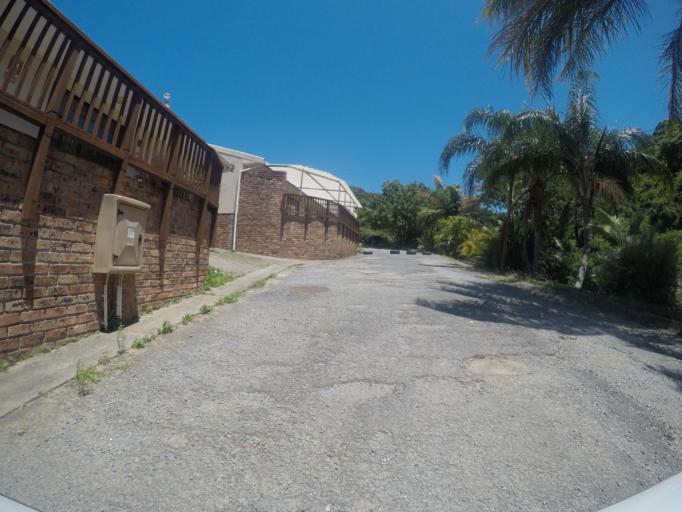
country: ZA
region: Eastern Cape
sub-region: Buffalo City Metropolitan Municipality
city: East London
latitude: -32.9351
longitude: 28.0088
